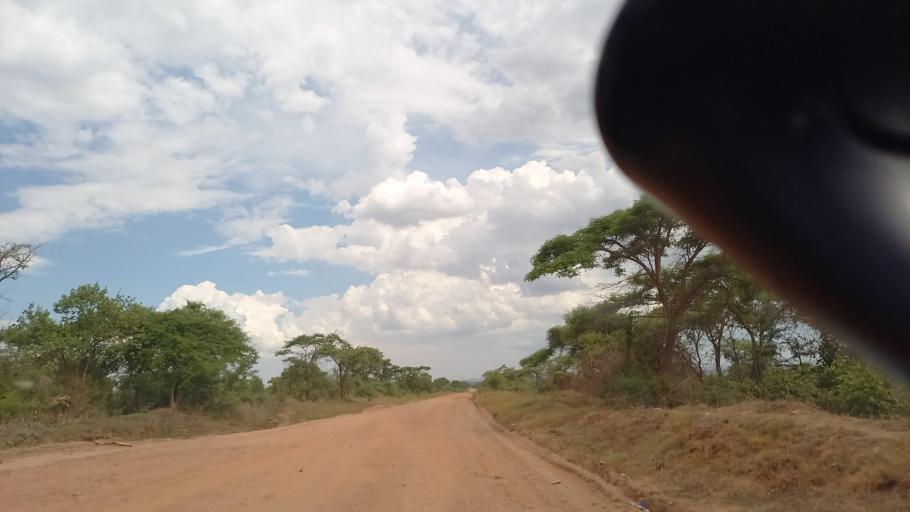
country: ZM
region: Southern
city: Nakambala
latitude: -16.0380
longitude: 27.9717
